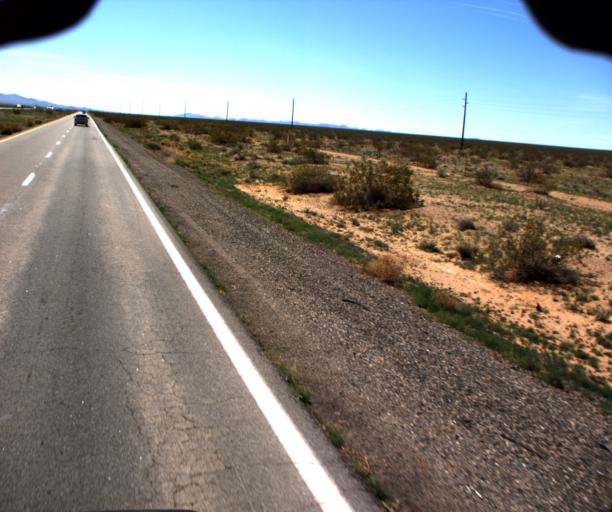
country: US
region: Arizona
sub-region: Mohave County
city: Dolan Springs
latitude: 35.6236
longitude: -114.4218
